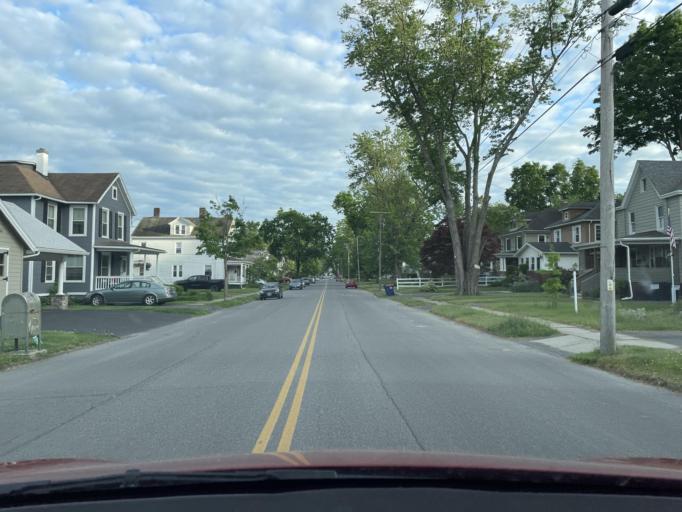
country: US
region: New York
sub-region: Ulster County
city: Saugerties
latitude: 42.0834
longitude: -73.9563
